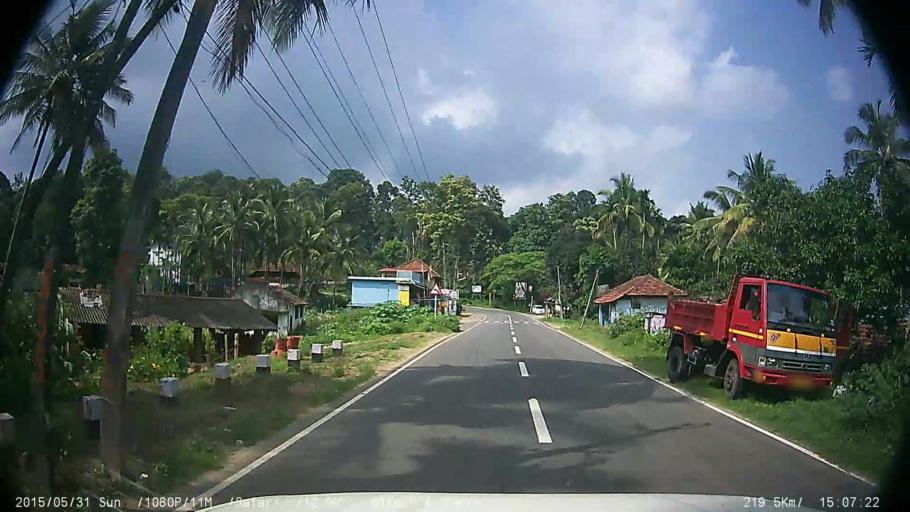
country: IN
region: Kerala
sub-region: Wayanad
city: Kalpetta
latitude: 11.6463
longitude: 76.2176
